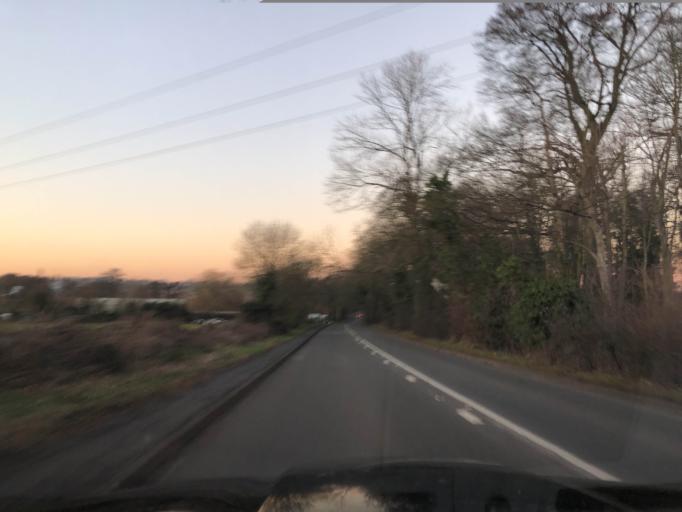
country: GB
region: England
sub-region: Warwickshire
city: Kenilworth
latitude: 52.3216
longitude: -1.5760
